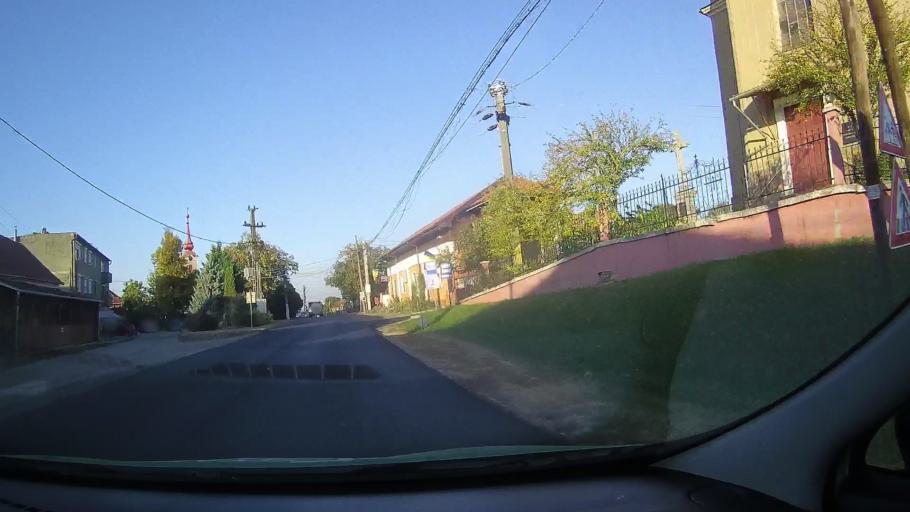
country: RO
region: Bihor
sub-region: Comuna Cetariu
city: Cetariu
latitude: 47.1428
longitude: 21.9982
